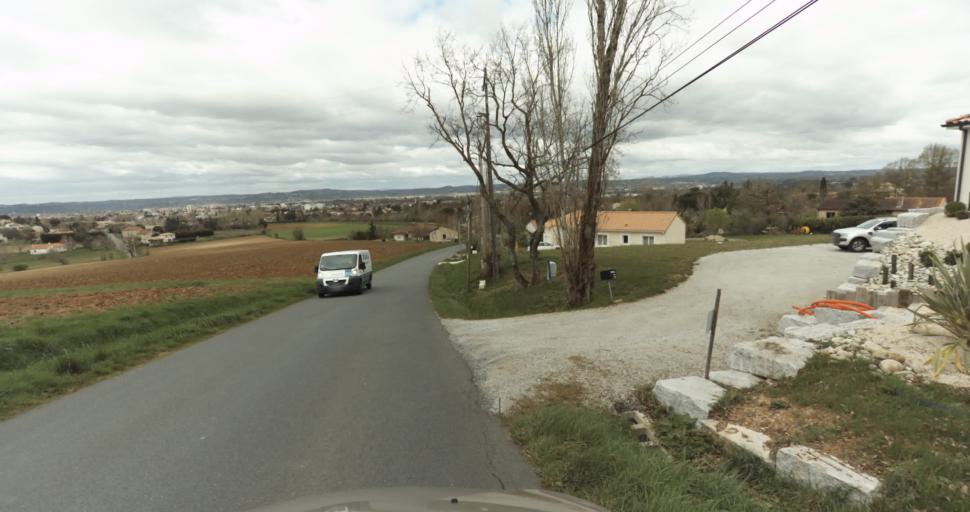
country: FR
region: Midi-Pyrenees
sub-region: Departement du Tarn
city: Puygouzon
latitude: 43.9047
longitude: 2.1722
